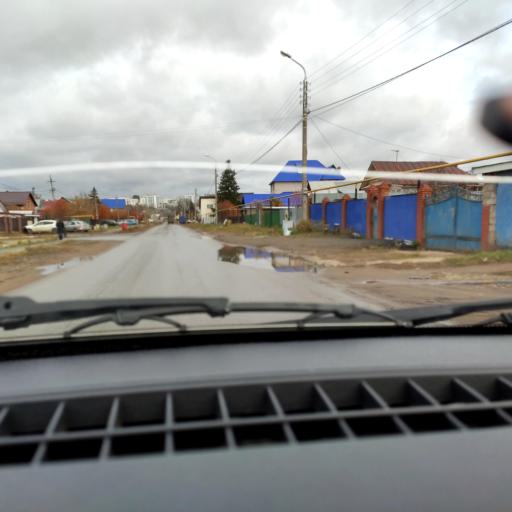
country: RU
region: Bashkortostan
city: Ufa
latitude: 54.6992
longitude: 55.9544
